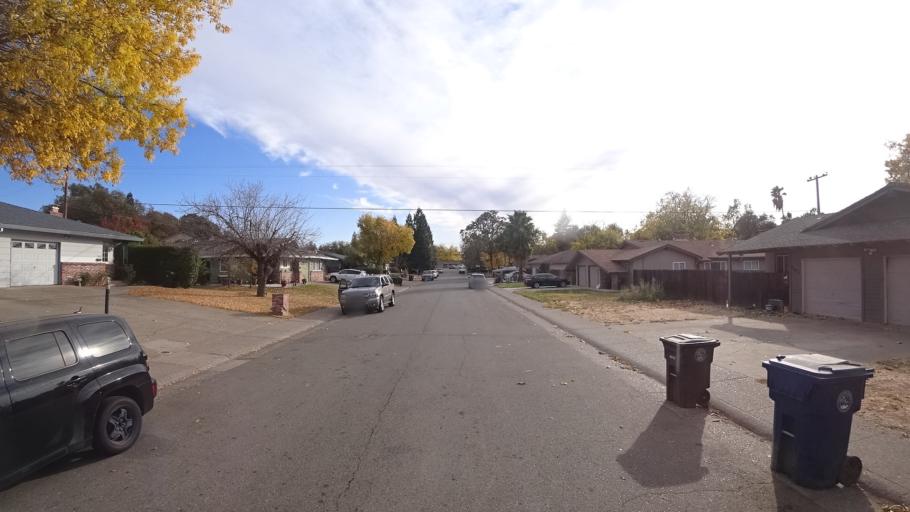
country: US
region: California
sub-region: Sacramento County
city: Citrus Heights
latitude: 38.7020
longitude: -121.2619
